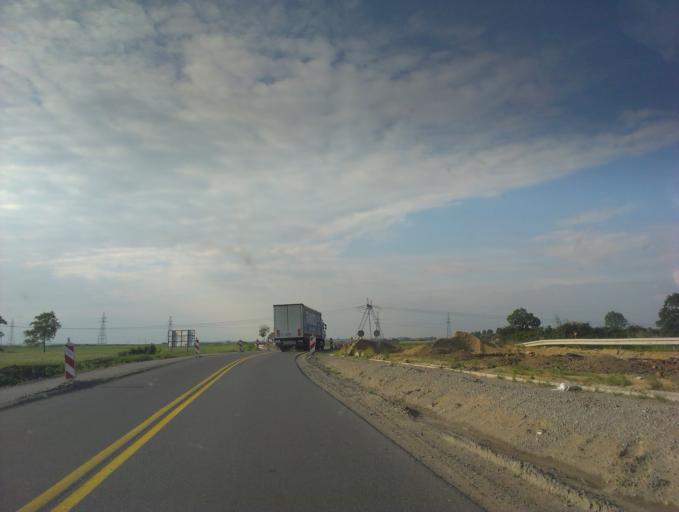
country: PL
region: Lower Silesian Voivodeship
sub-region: Powiat trzebnicki
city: Psary
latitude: 51.2198
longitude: 17.0399
